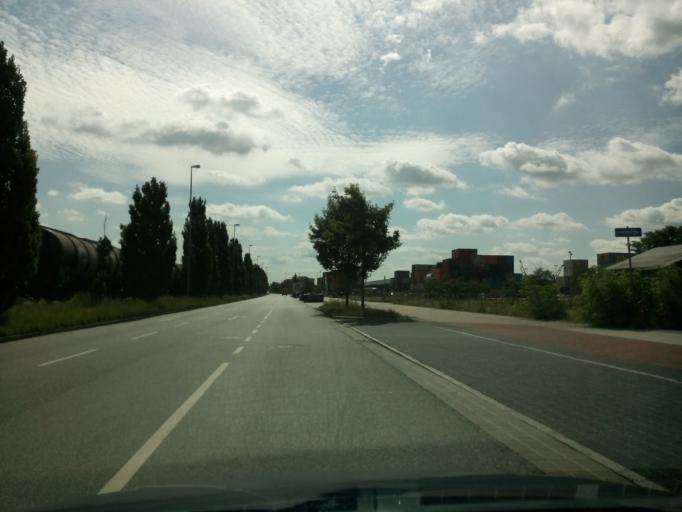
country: DE
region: Lower Saxony
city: Ritterhude
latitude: 53.1267
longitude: 8.7334
